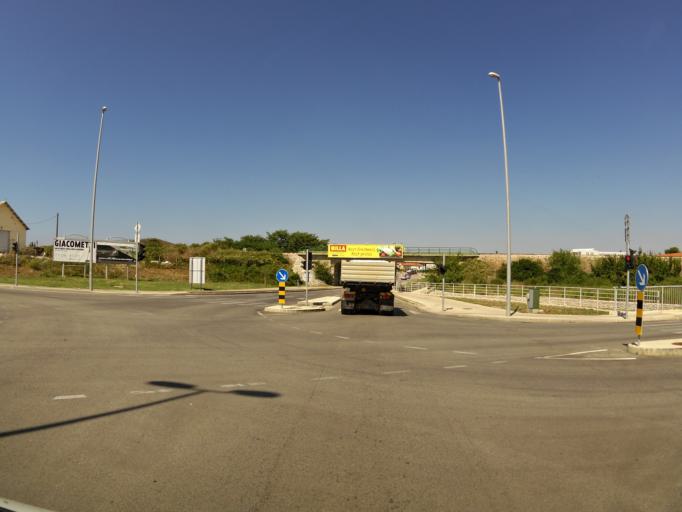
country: HR
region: Zadarska
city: Zadar
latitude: 44.0994
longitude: 15.2557
